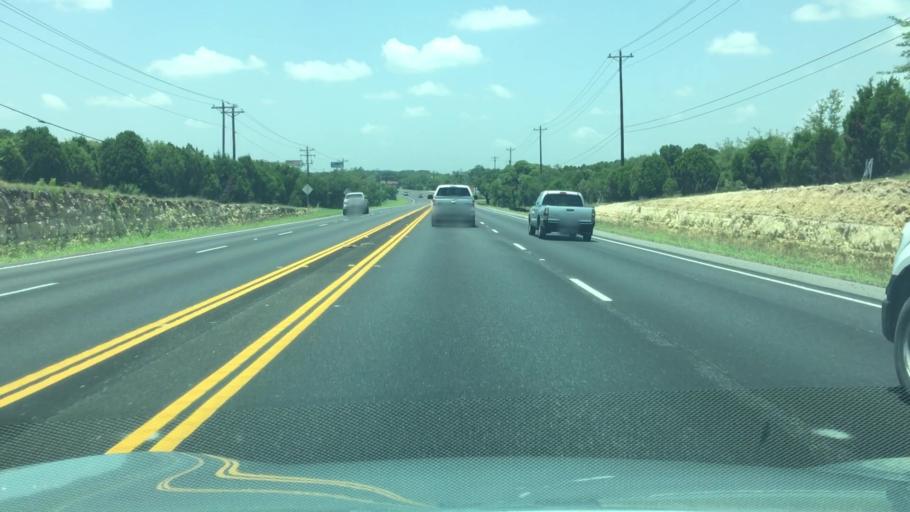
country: US
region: Texas
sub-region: Travis County
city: Barton Creek
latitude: 30.2325
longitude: -97.9049
